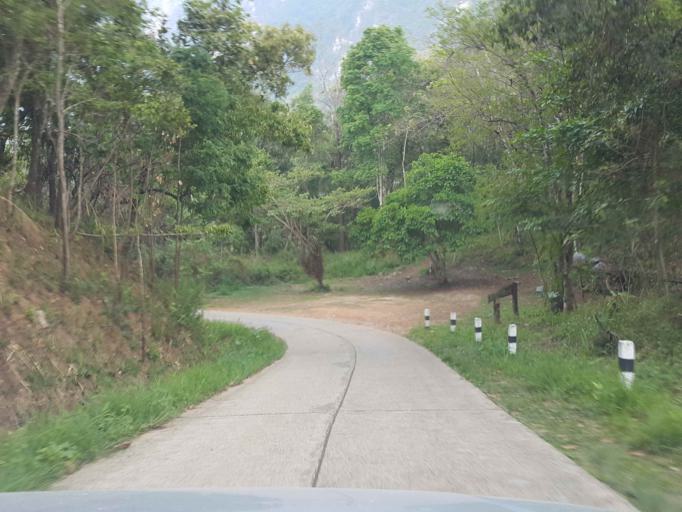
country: TH
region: Chiang Mai
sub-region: Amphoe Chiang Dao
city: Chiang Dao
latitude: 19.4129
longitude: 98.8586
